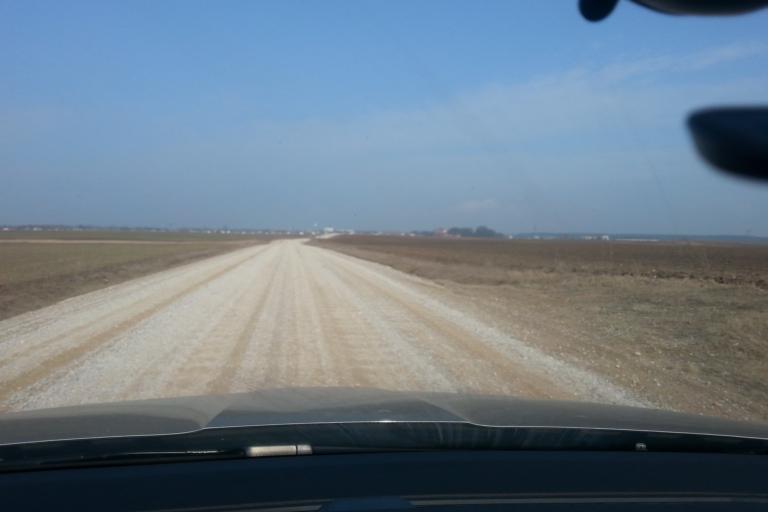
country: LT
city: Trakai
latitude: 54.5928
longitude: 24.9776
